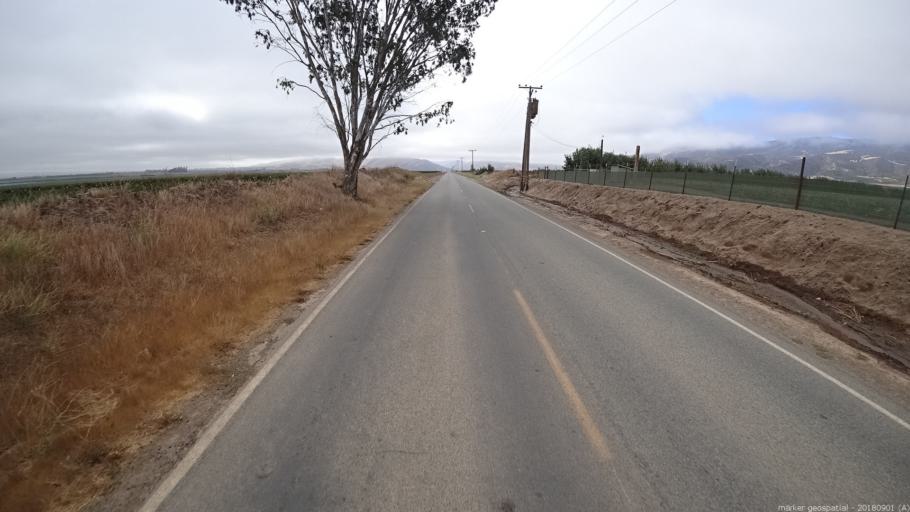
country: US
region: California
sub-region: Monterey County
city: Greenfield
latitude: 36.3412
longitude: -121.3185
